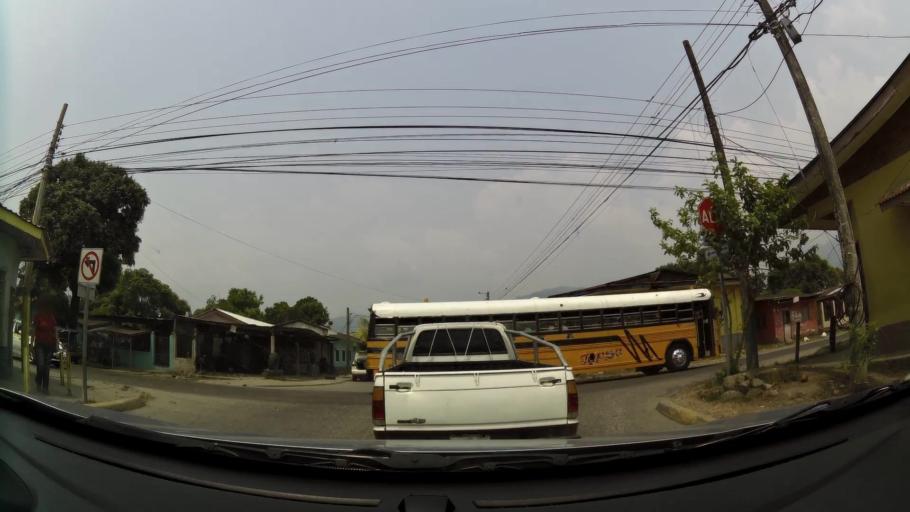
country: HN
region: Yoro
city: El Progreso
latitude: 15.4001
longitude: -87.8050
